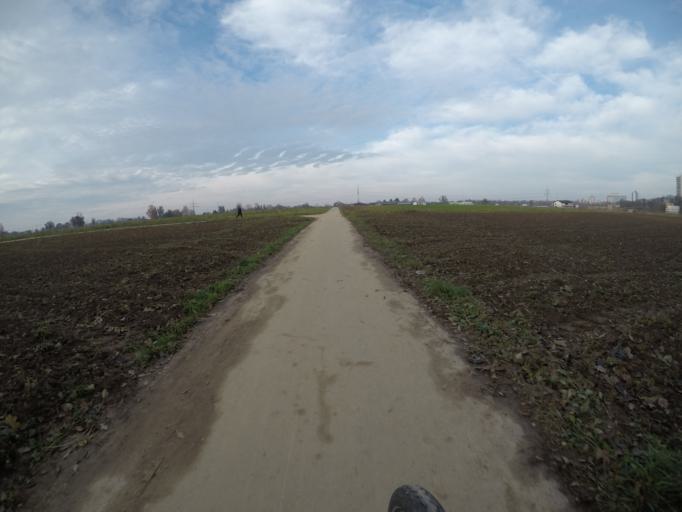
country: DE
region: Baden-Wuerttemberg
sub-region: Regierungsbezirk Stuttgart
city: Leinfelden-Echterdingen
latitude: 48.7117
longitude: 9.1458
